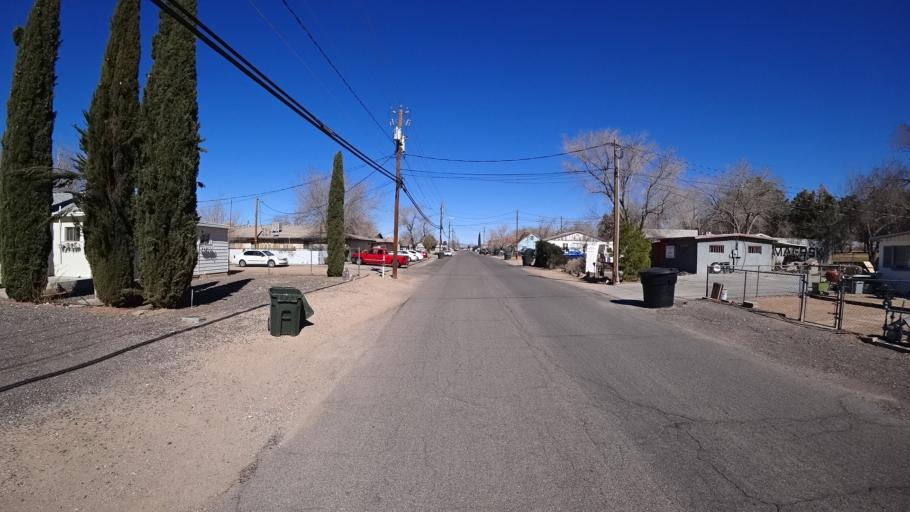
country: US
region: Arizona
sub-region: Mohave County
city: Kingman
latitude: 35.2003
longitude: -114.0279
